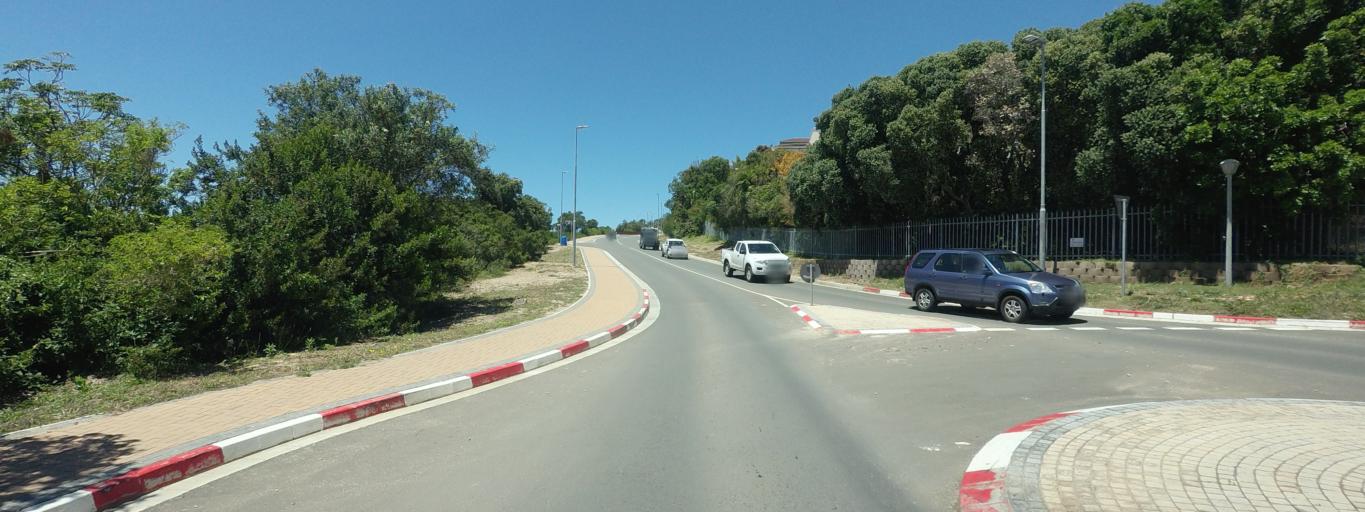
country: ZA
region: Western Cape
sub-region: Eden District Municipality
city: Plettenberg Bay
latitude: -34.0477
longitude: 23.3694
